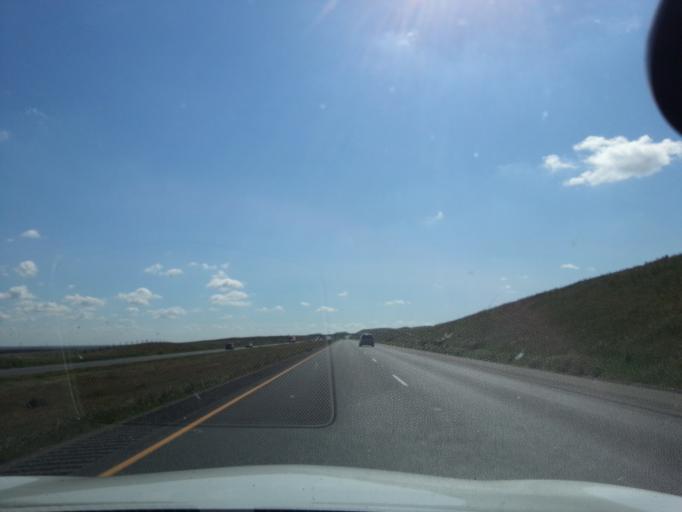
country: US
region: California
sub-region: Fresno County
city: Coalinga
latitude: 36.3379
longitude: -120.3069
